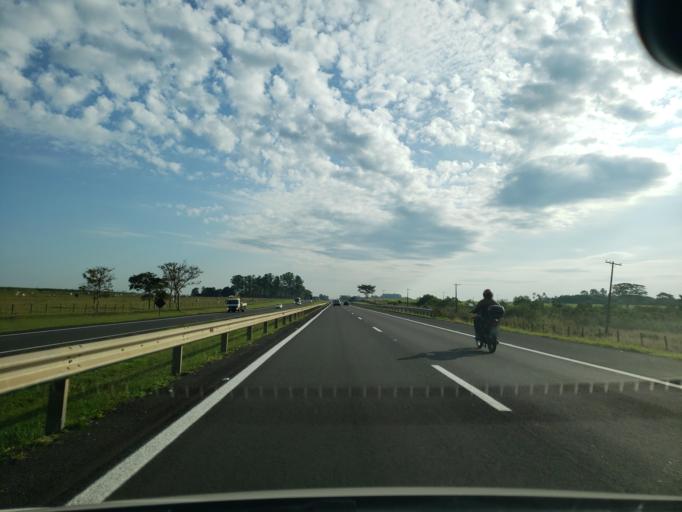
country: BR
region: Sao Paulo
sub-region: Guararapes
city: Guararapes
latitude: -21.2016
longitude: -50.5888
